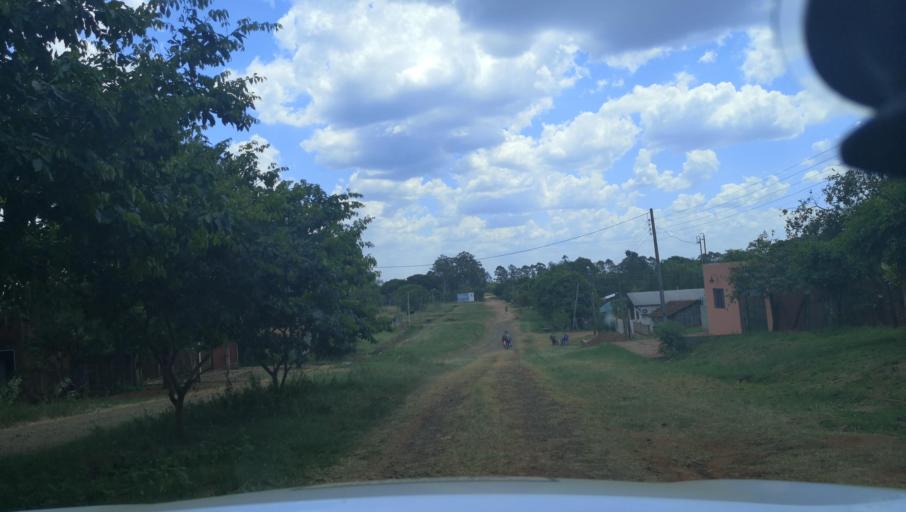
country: PY
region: Itapua
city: Carmen del Parana
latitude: -27.1717
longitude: -56.2348
